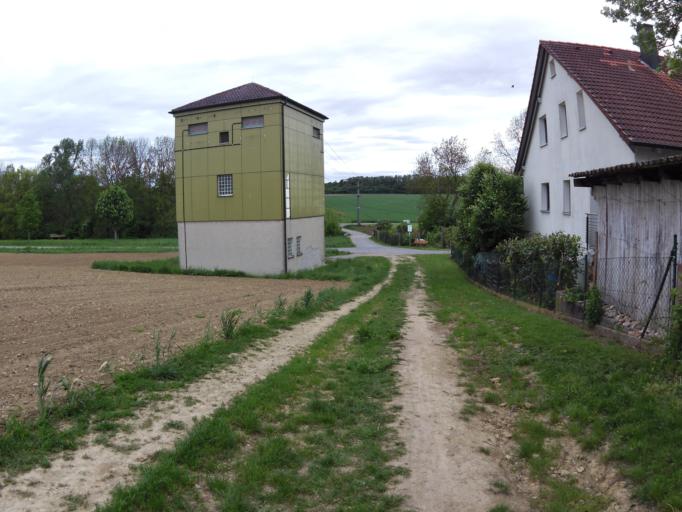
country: DE
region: Bavaria
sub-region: Regierungsbezirk Unterfranken
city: Kurnach
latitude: 49.8463
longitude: 10.0508
